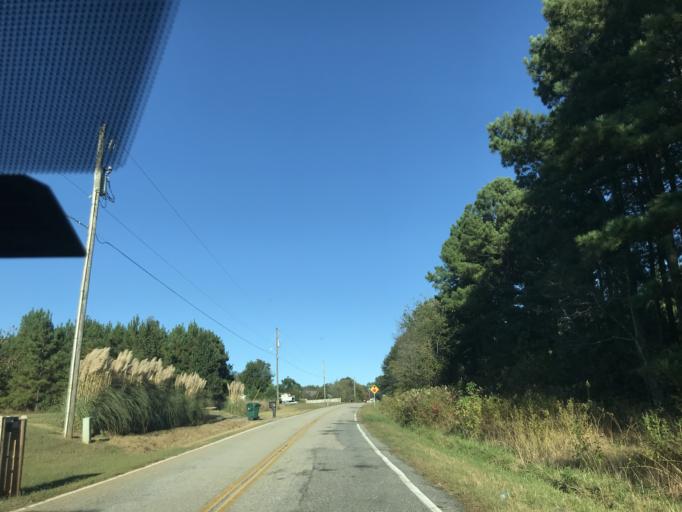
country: US
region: South Carolina
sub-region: Spartanburg County
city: Mayo
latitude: 35.1259
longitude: -81.7862
